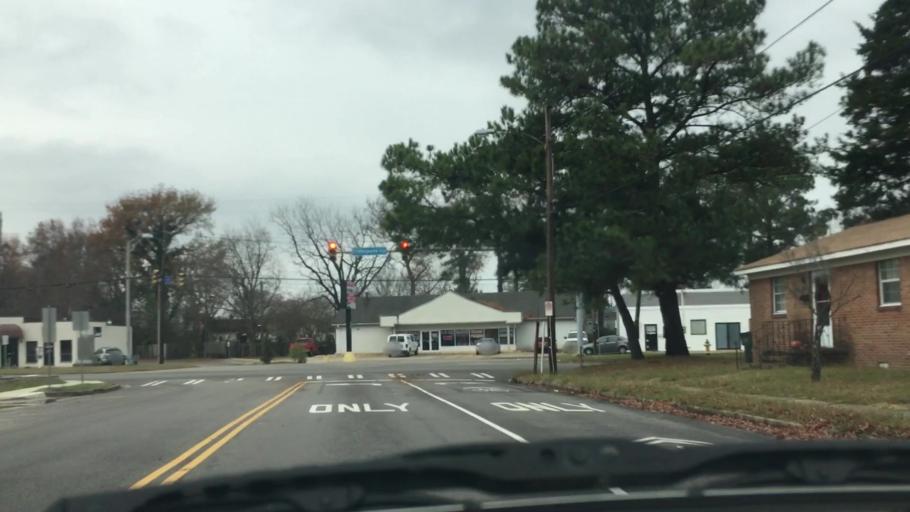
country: US
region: Virginia
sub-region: City of Norfolk
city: Norfolk
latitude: 36.8785
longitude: -76.2491
